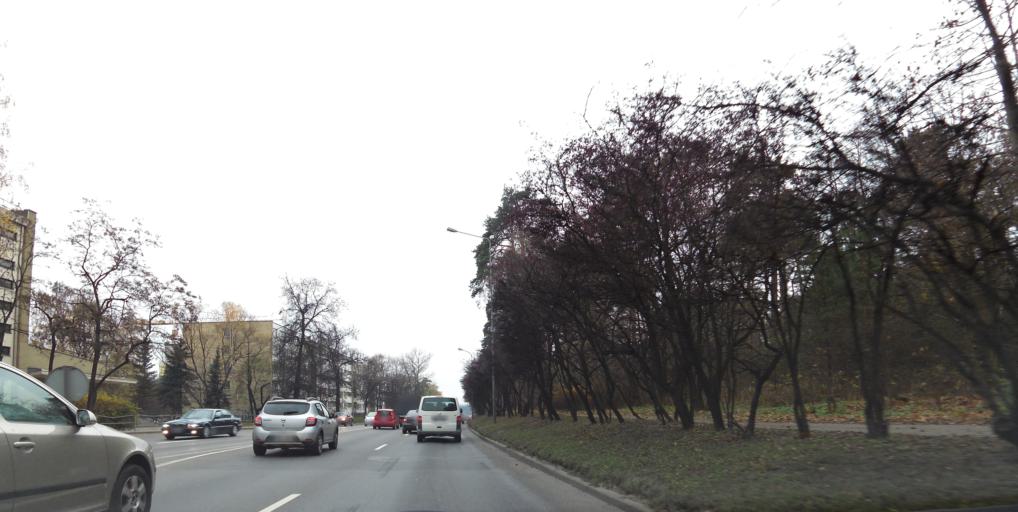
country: LT
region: Vilnius County
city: Vilkpede
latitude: 54.6758
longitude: 25.2447
